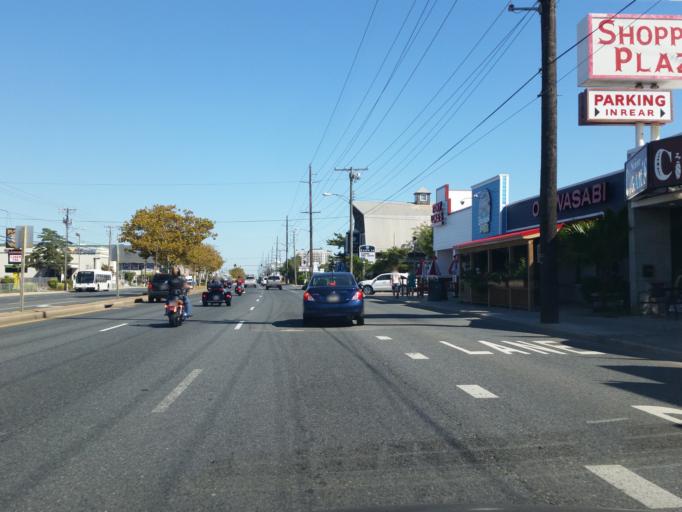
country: US
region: Maryland
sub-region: Worcester County
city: Ocean City
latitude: 38.3618
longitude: -75.0728
